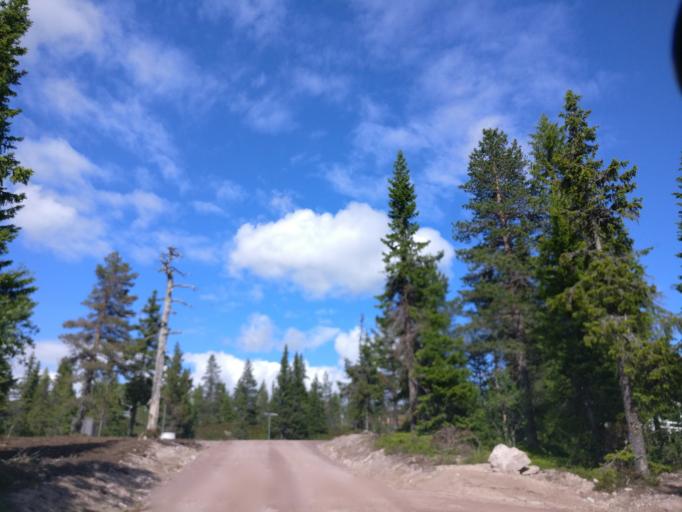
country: SE
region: Dalarna
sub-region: Malung-Saelens kommun
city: Malung
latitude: 61.1683
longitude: 13.0958
